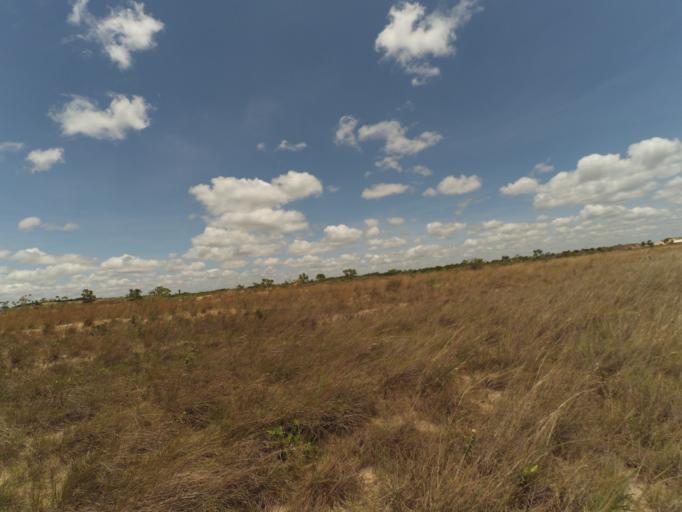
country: BO
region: Santa Cruz
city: Santa Cruz de la Sierra
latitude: -17.9382
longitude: -63.1595
